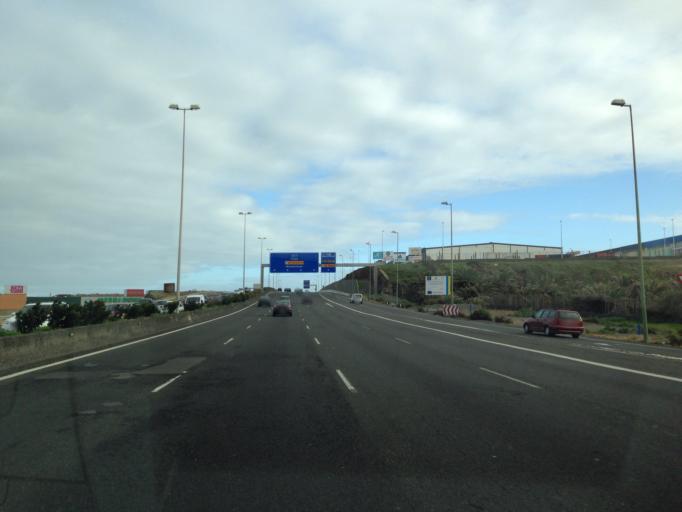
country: ES
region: Canary Islands
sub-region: Provincia de Las Palmas
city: Telde
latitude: 28.0298
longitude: -15.3991
